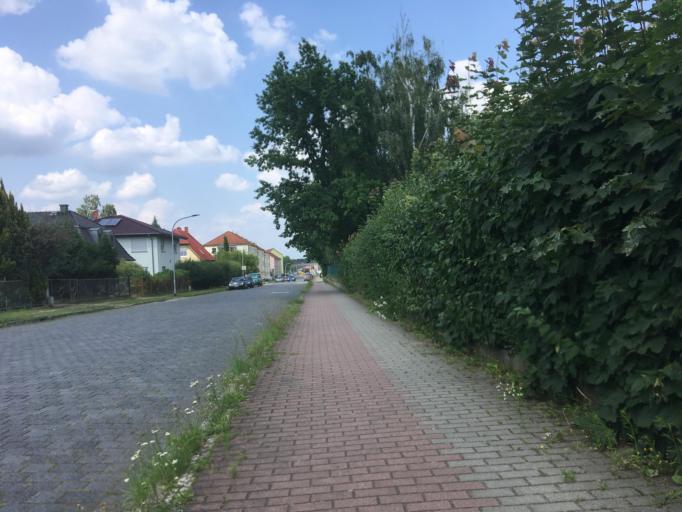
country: DE
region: Brandenburg
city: Wildau
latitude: 52.3205
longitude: 13.6224
